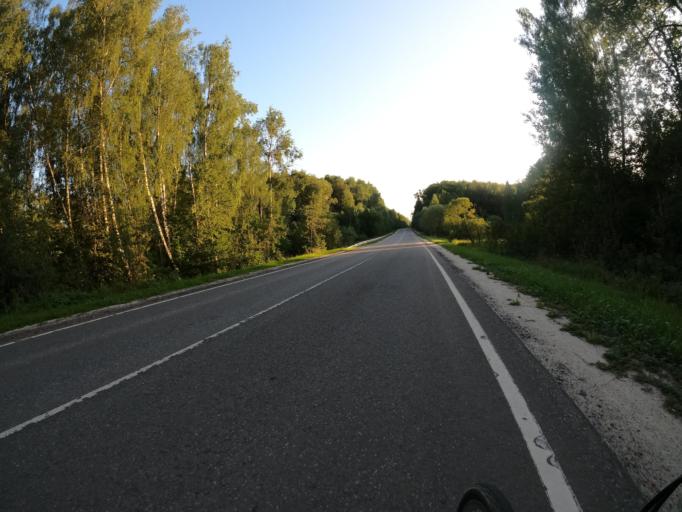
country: RU
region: Moskovskaya
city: Meshcherino
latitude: 55.1104
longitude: 38.3085
